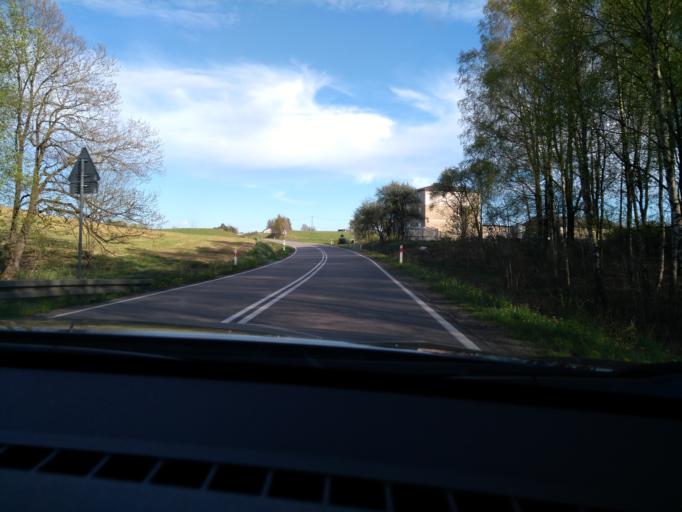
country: PL
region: Pomeranian Voivodeship
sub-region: Powiat leborski
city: Cewice
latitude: 54.3355
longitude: 17.7098
